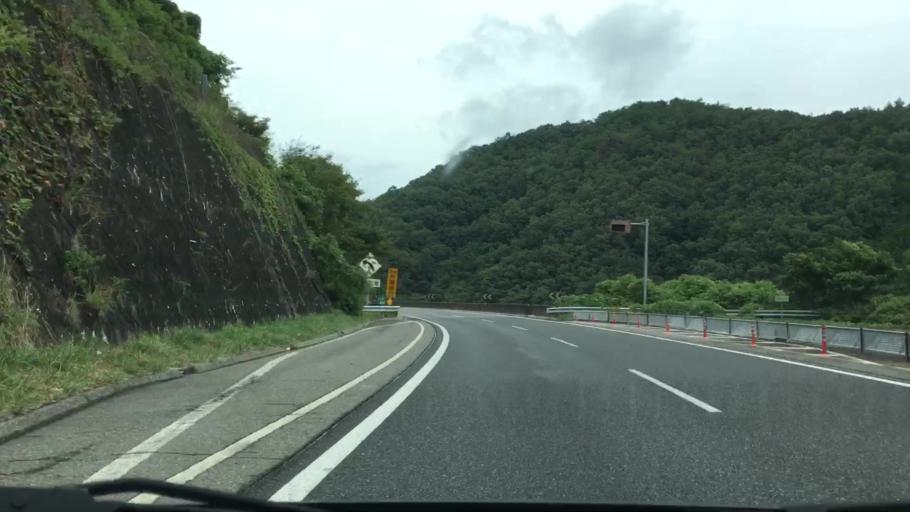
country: JP
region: Okayama
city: Niimi
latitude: 34.9941
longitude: 133.6066
